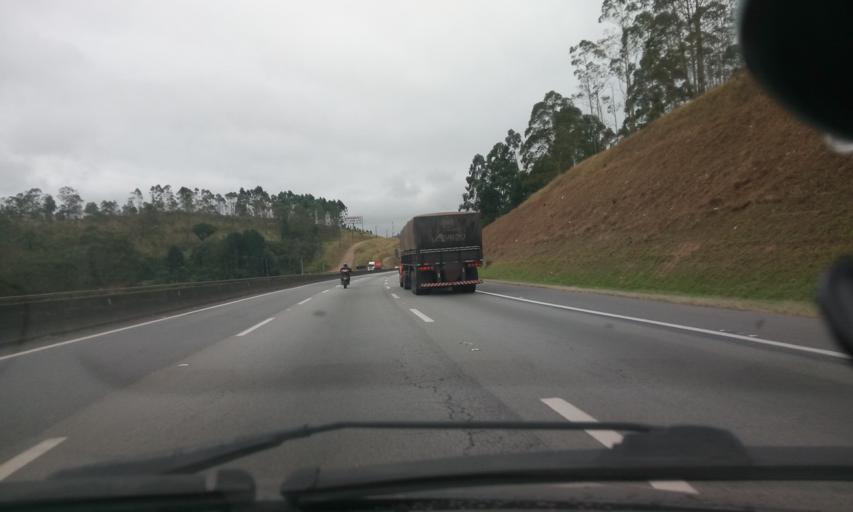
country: BR
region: Sao Paulo
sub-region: Itapecerica Da Serra
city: Itapecerica da Serra
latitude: -23.7373
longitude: -46.8131
